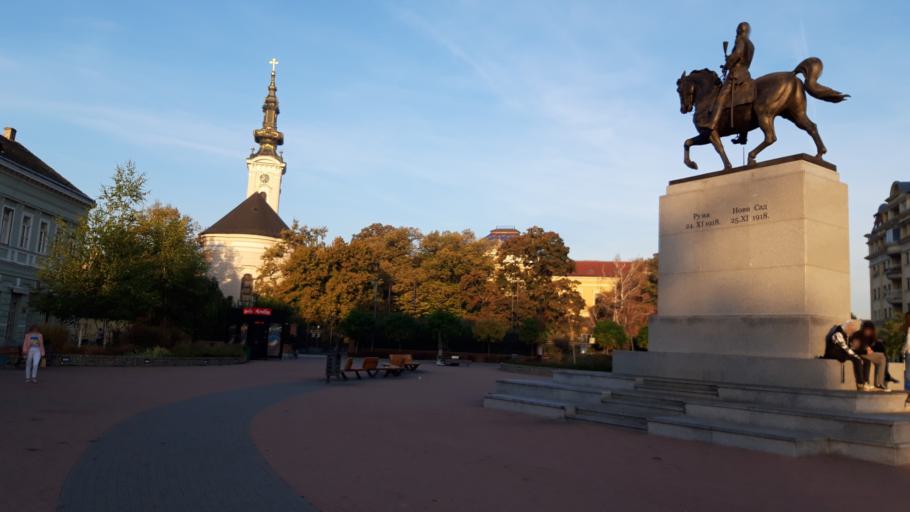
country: RS
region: Autonomna Pokrajina Vojvodina
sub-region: Juznobacki Okrug
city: Novi Sad
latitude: 45.2576
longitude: 19.8494
